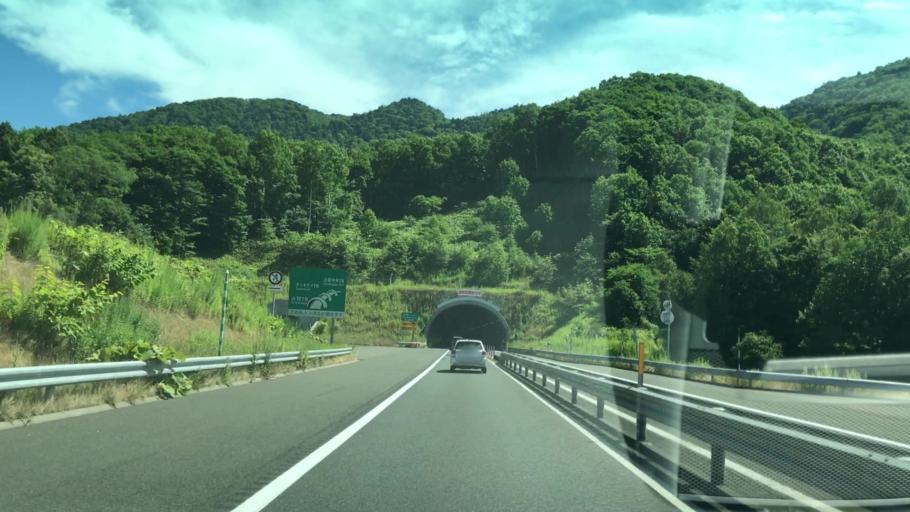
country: JP
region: Hokkaido
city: Shimo-furano
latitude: 42.9570
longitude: 142.3332
